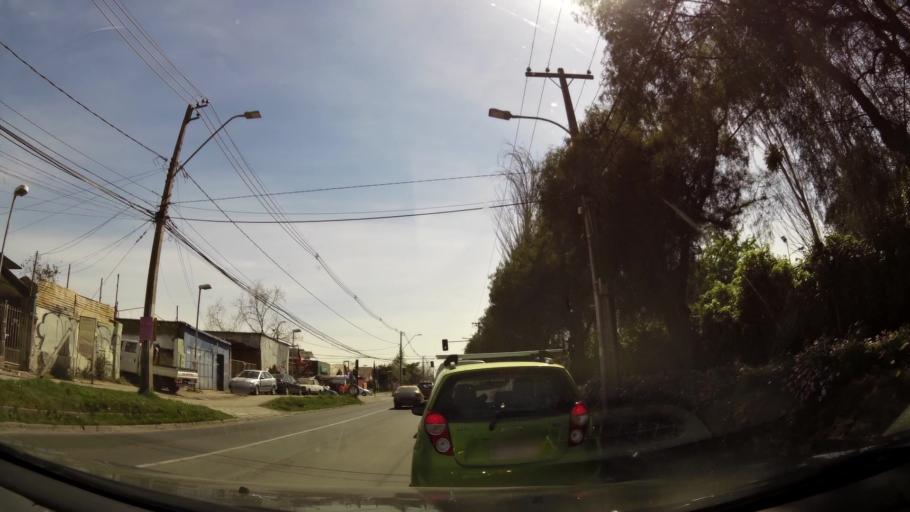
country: CL
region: Santiago Metropolitan
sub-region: Provincia de Cordillera
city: Puente Alto
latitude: -33.6206
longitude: -70.5739
